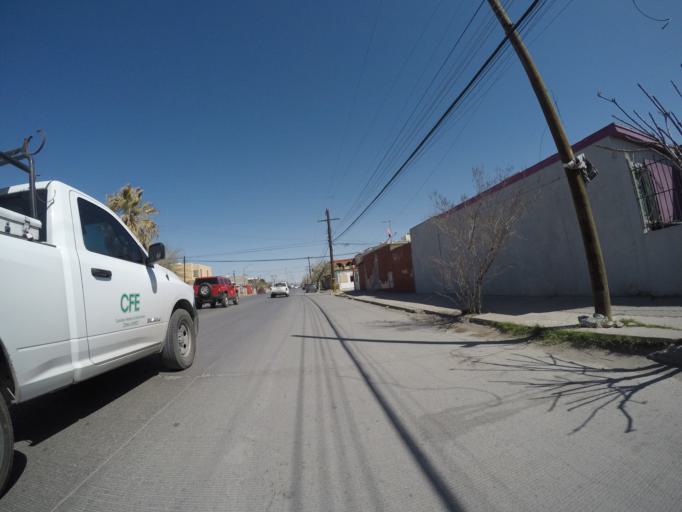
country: MX
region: Chihuahua
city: Ciudad Juarez
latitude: 31.7076
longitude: -106.4468
